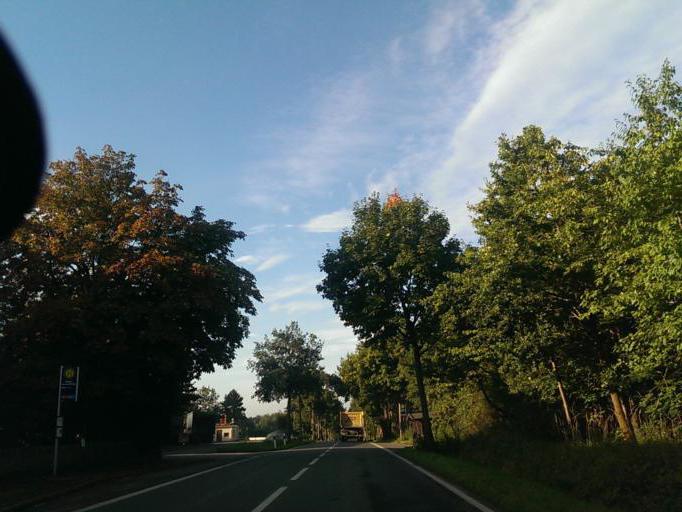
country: DE
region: Lower Saxony
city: Lindwedel
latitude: 52.5608
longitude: 9.6901
